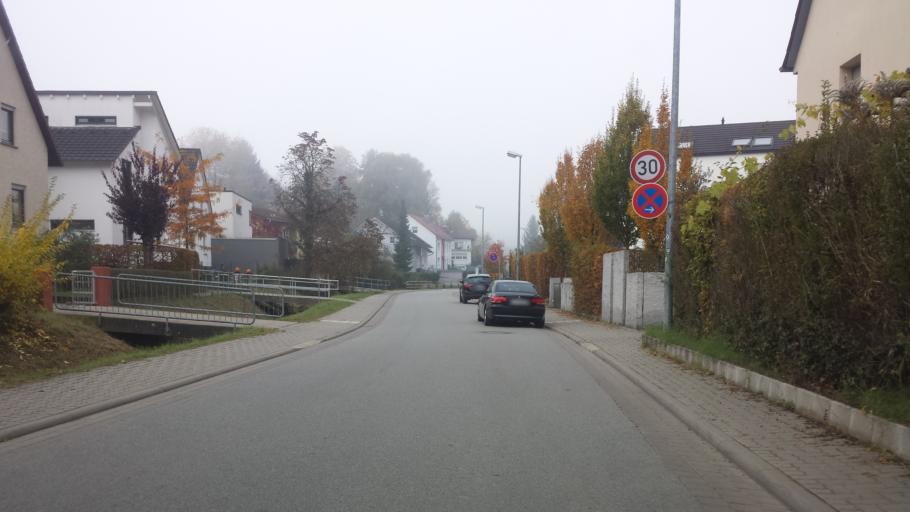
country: DE
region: Hesse
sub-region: Regierungsbezirk Darmstadt
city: Bensheim
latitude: 49.6828
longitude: 8.6656
